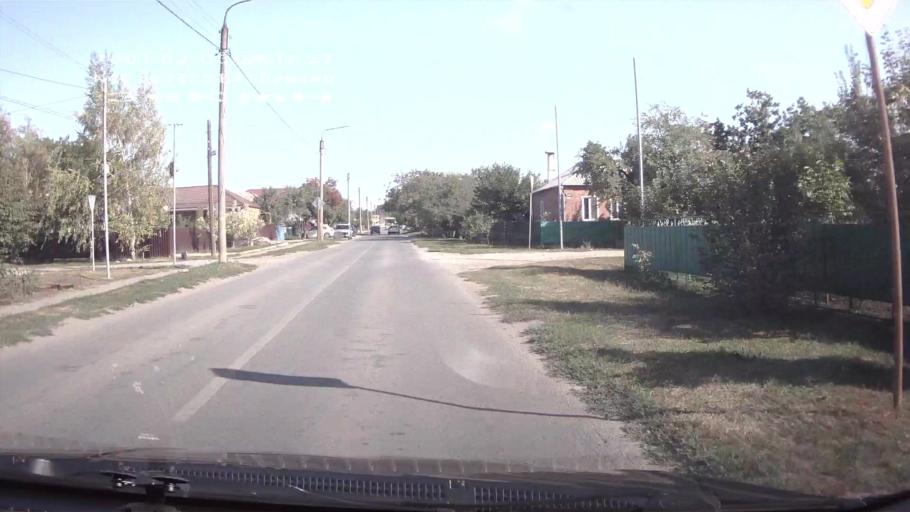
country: RU
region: Rostov
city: Tselina
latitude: 46.5329
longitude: 41.0264
